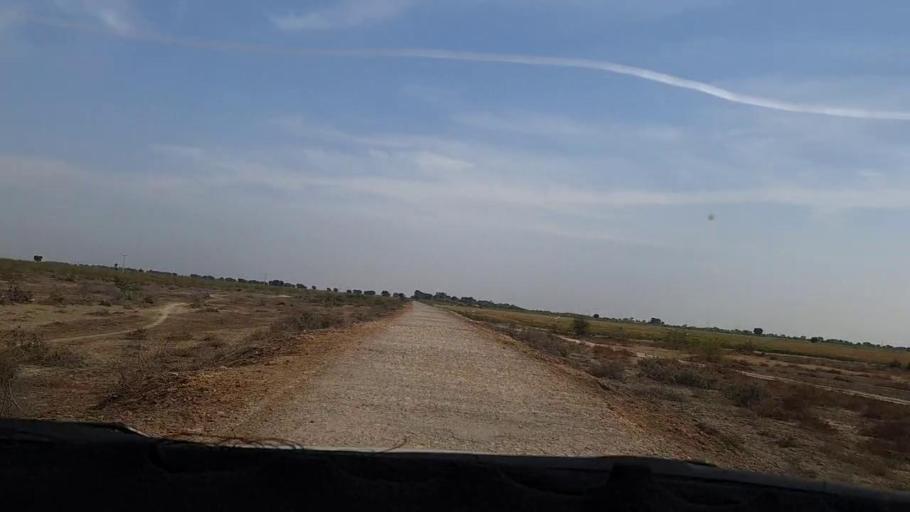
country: PK
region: Sindh
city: Pithoro
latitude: 25.5402
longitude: 69.3342
